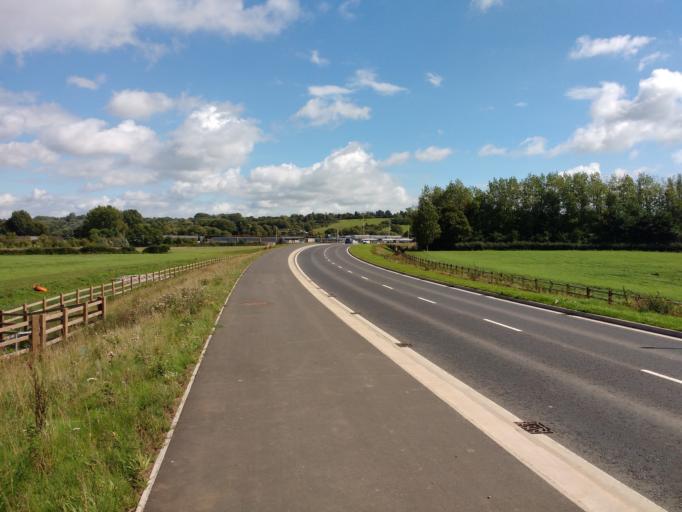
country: GB
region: England
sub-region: North Somerset
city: Long Ashton
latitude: 51.4320
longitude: -2.6378
